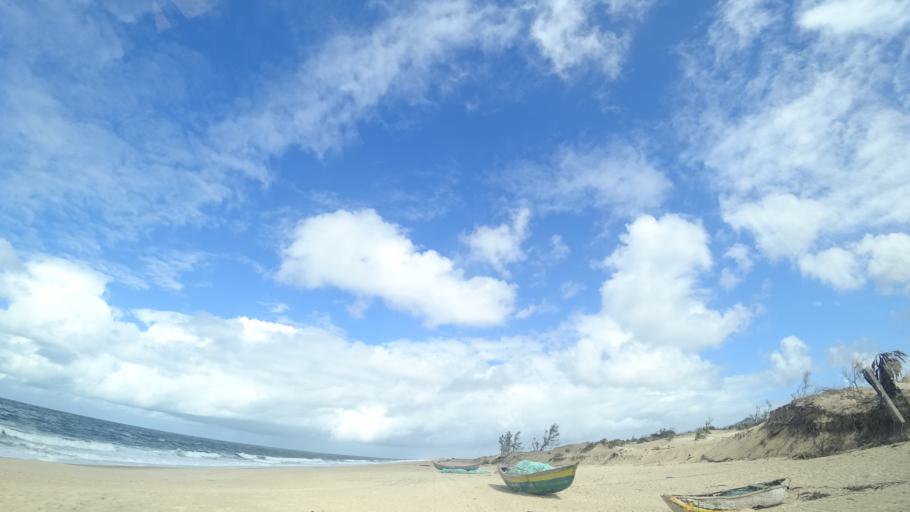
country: MZ
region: Sofala
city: Beira
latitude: -19.6470
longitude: 35.1831
